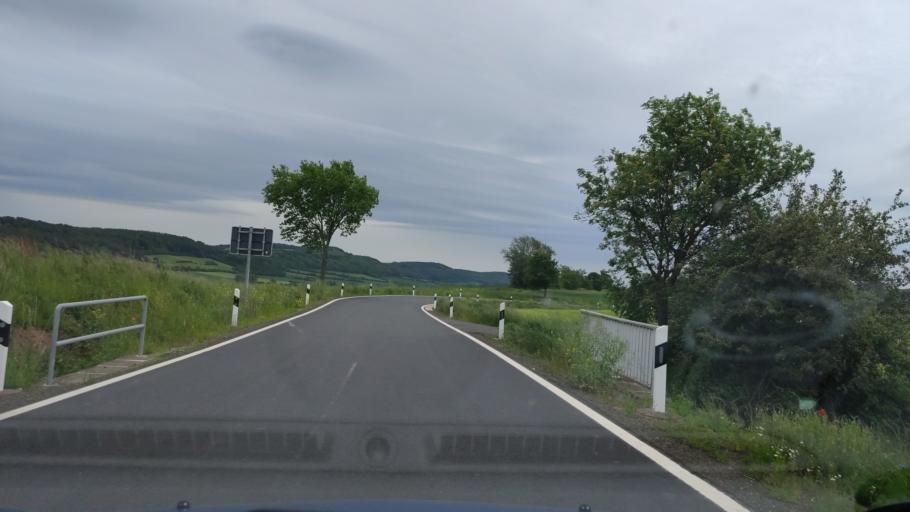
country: DE
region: Lower Saxony
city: Hardegsen
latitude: 51.7076
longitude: 9.7841
